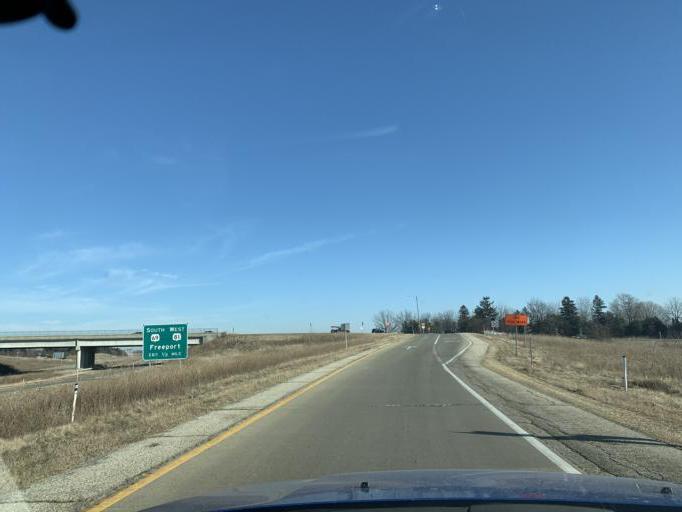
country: US
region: Wisconsin
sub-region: Green County
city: Monroe
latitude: 42.6044
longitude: -89.6666
